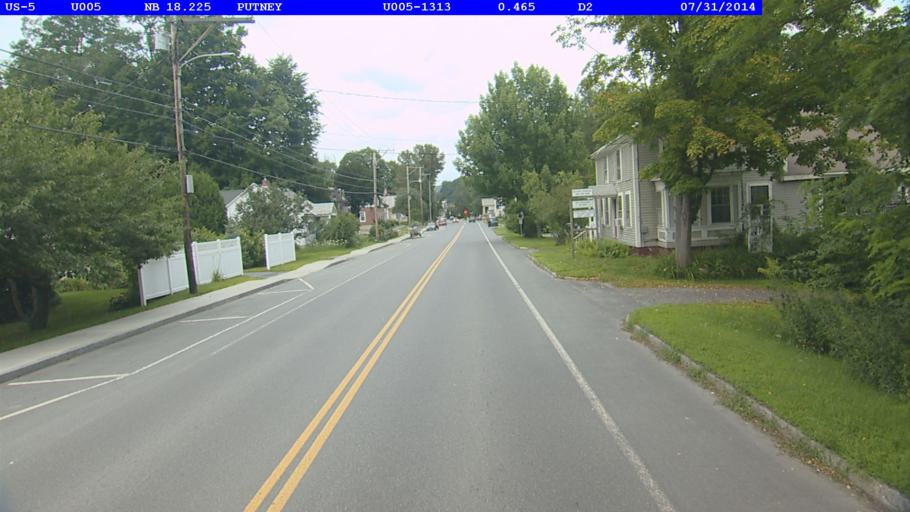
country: US
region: New Hampshire
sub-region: Cheshire County
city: Westmoreland
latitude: 42.9722
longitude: -72.5221
